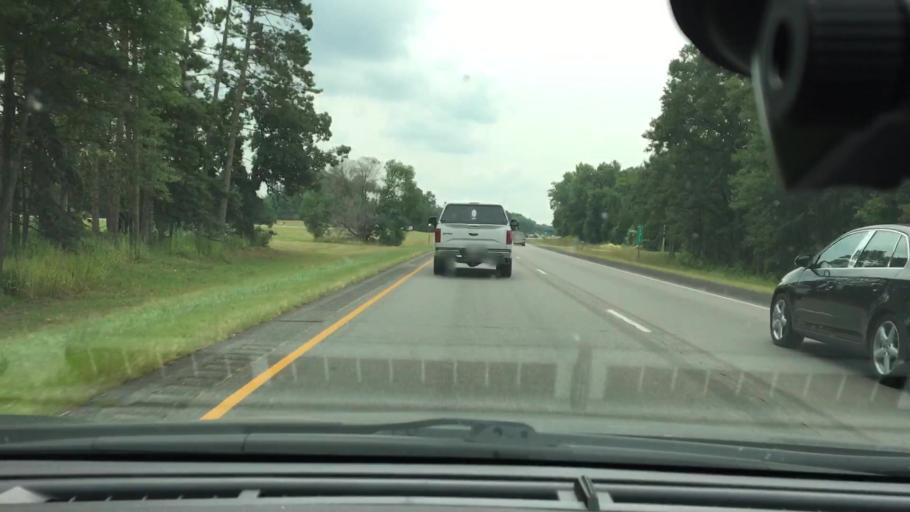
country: US
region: Minnesota
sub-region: Sherburne County
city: Zimmerman
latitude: 45.4697
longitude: -93.5829
